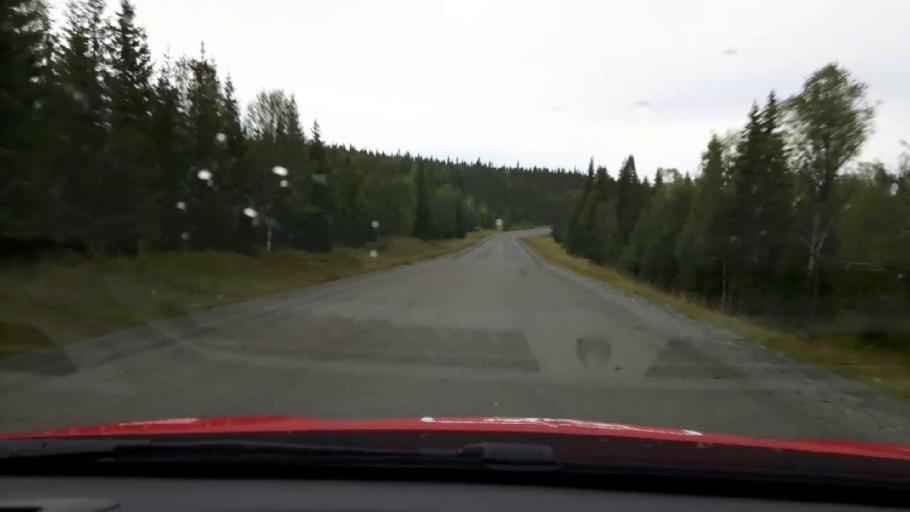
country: SE
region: Jaemtland
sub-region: Are Kommun
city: Are
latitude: 63.4155
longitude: 12.7608
